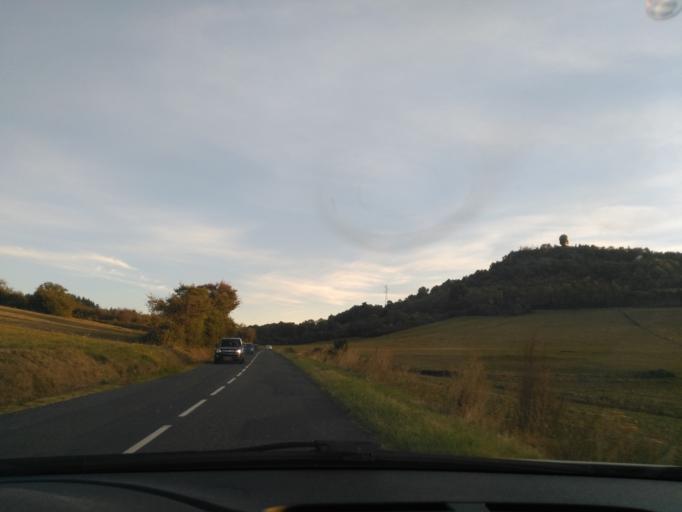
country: FR
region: Rhone-Alpes
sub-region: Departement du Rhone
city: Limonest
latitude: 45.8359
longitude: 4.7936
